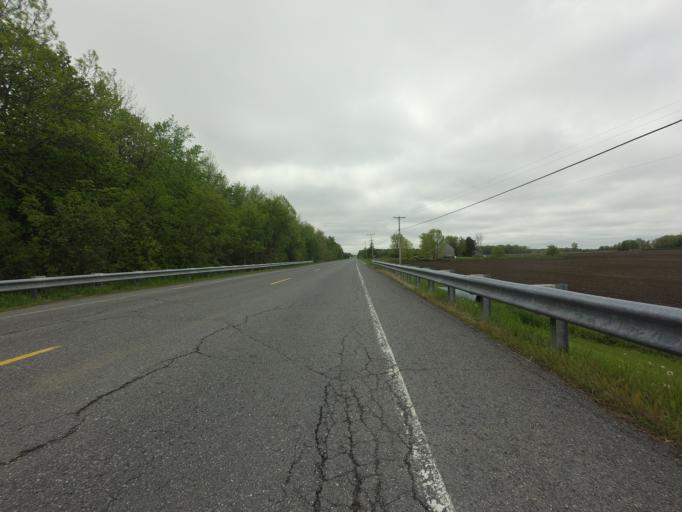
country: CA
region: Ontario
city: Casselman
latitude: 45.0476
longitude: -75.1971
